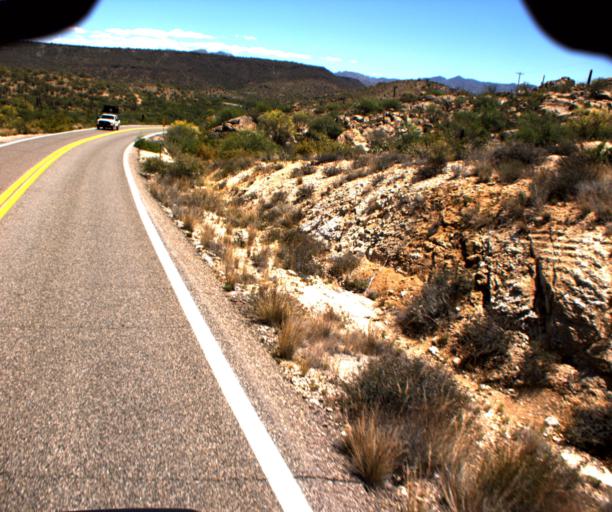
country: US
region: Arizona
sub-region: Yavapai County
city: Bagdad
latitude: 34.5186
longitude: -113.0941
